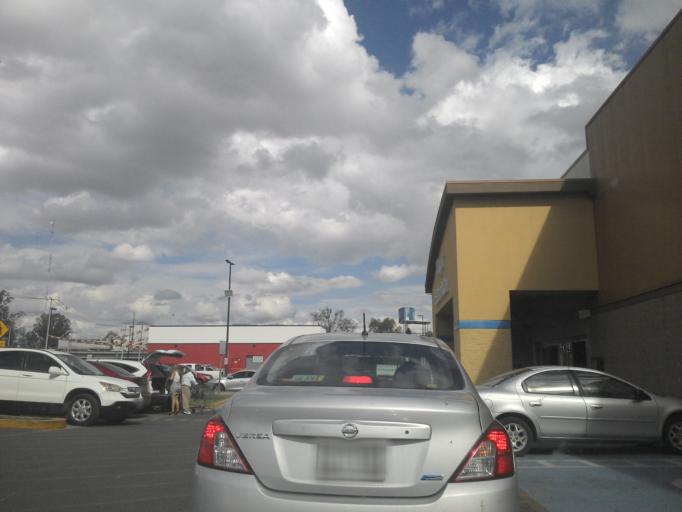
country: MX
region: Jalisco
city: Guadalajara
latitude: 20.6574
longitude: -103.4491
